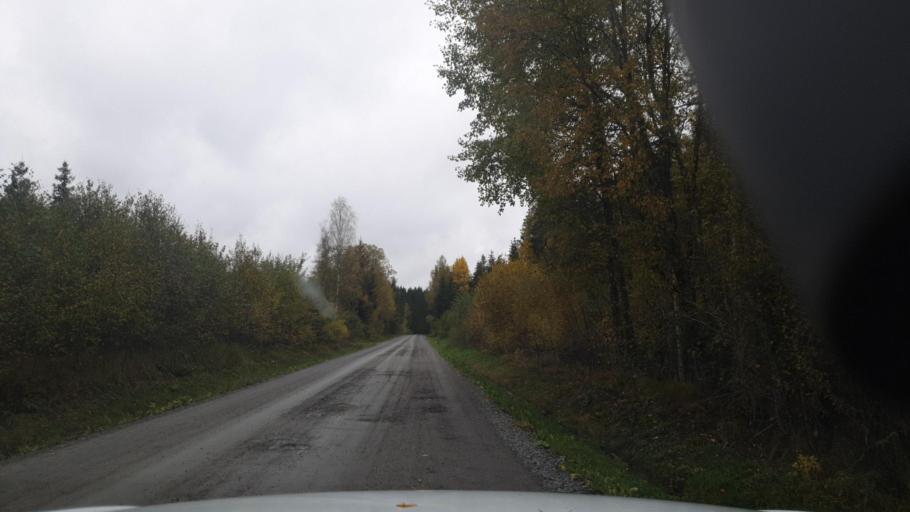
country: SE
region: Vaermland
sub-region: Karlstads Kommun
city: Edsvalla
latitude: 59.4428
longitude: 13.1958
